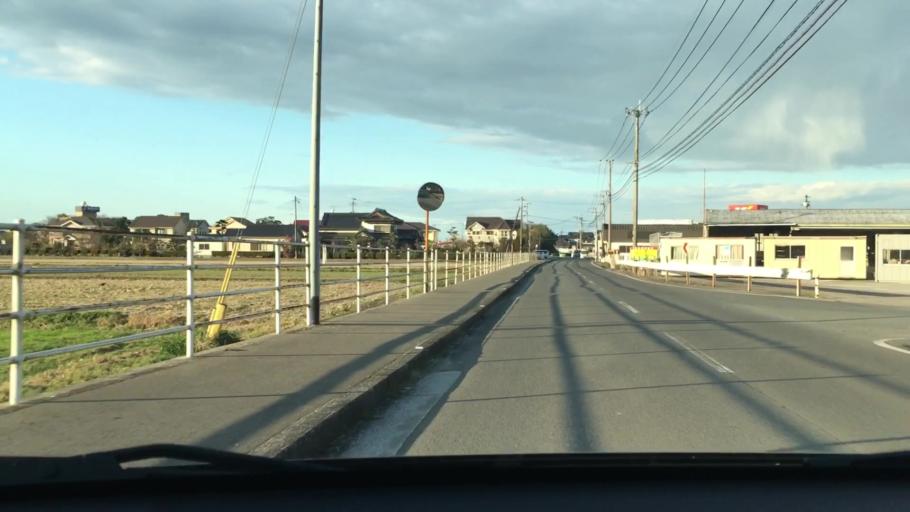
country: JP
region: Oita
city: Bungo-Takada-shi
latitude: 33.5197
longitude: 131.3482
